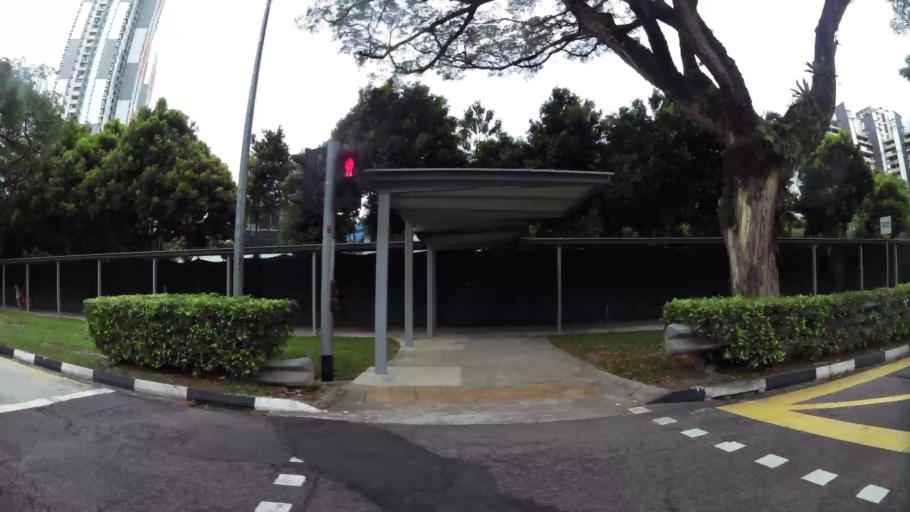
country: SG
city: Singapore
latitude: 1.3081
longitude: 103.7876
